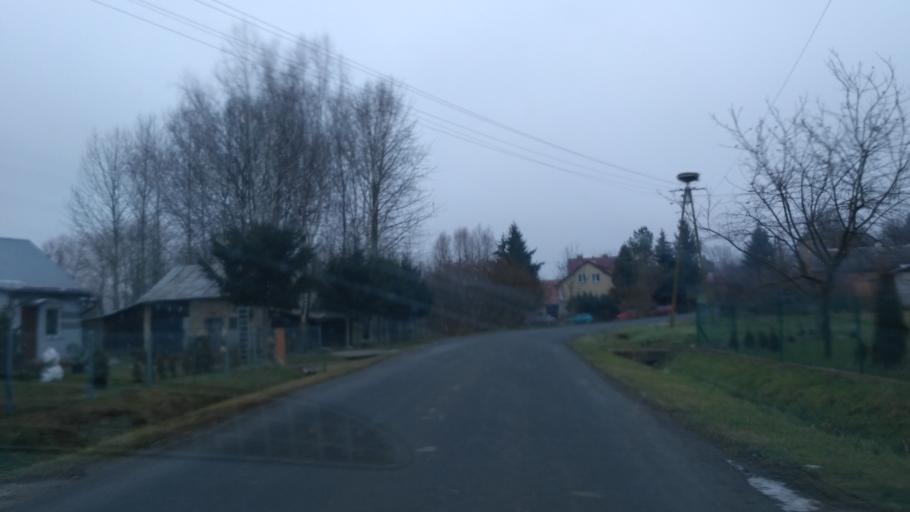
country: PL
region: Subcarpathian Voivodeship
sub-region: Powiat przeworski
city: Zarzecze
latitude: 49.9564
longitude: 22.5662
